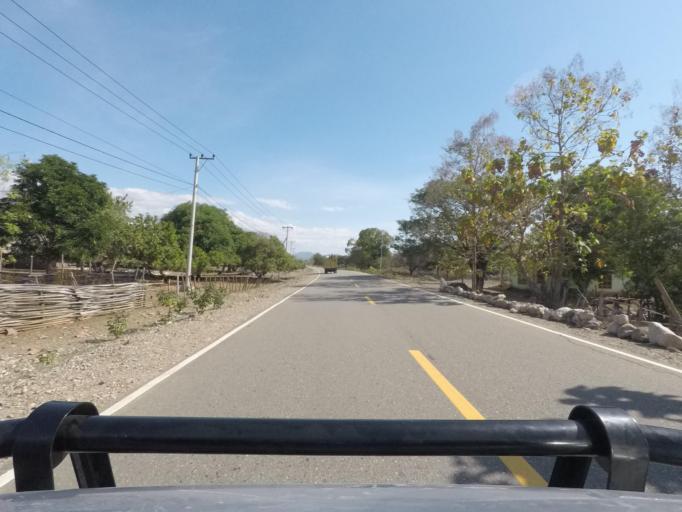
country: ID
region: East Nusa Tenggara
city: Atambua
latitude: -8.9251
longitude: 124.9881
